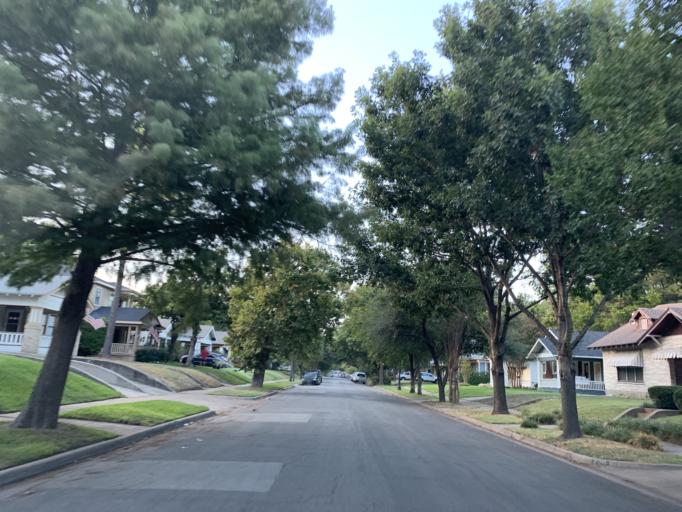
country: US
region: Texas
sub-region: Dallas County
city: Cockrell Hill
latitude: 32.7466
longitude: -96.8417
